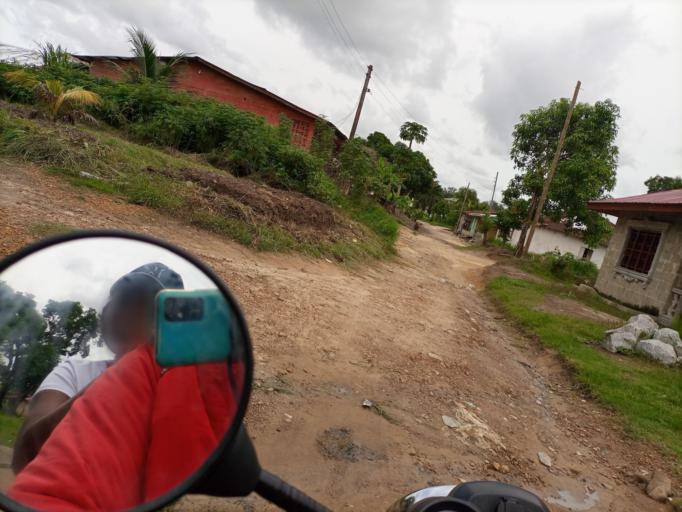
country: SL
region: Southern Province
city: Bo
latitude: 7.9539
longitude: -11.7459
